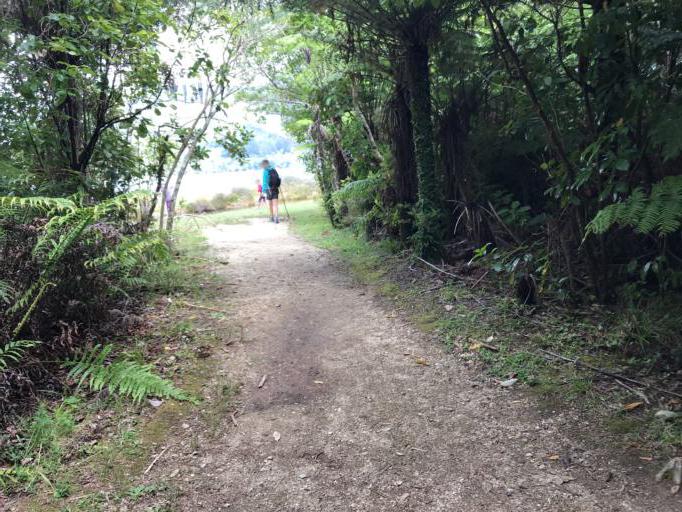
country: NZ
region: Marlborough
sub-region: Marlborough District
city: Picton
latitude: -41.2537
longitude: 173.9407
